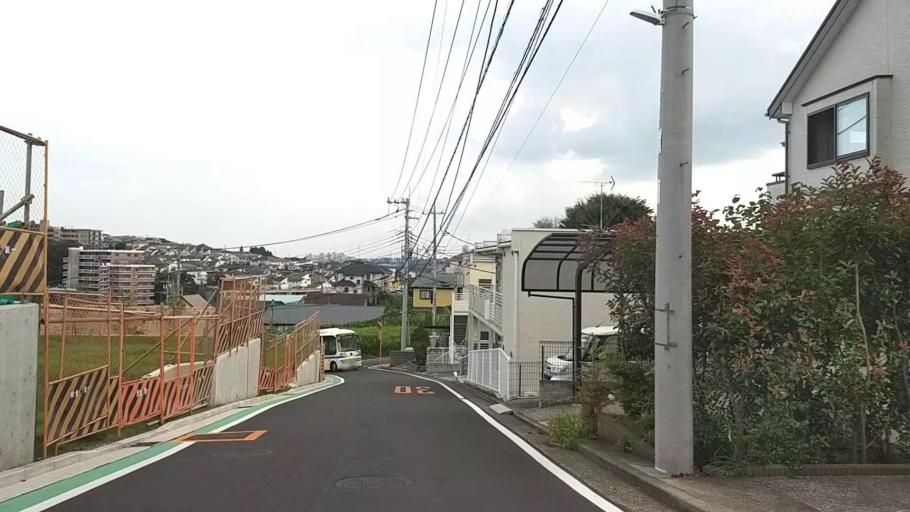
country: JP
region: Kanagawa
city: Yokohama
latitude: 35.4822
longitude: 139.5687
